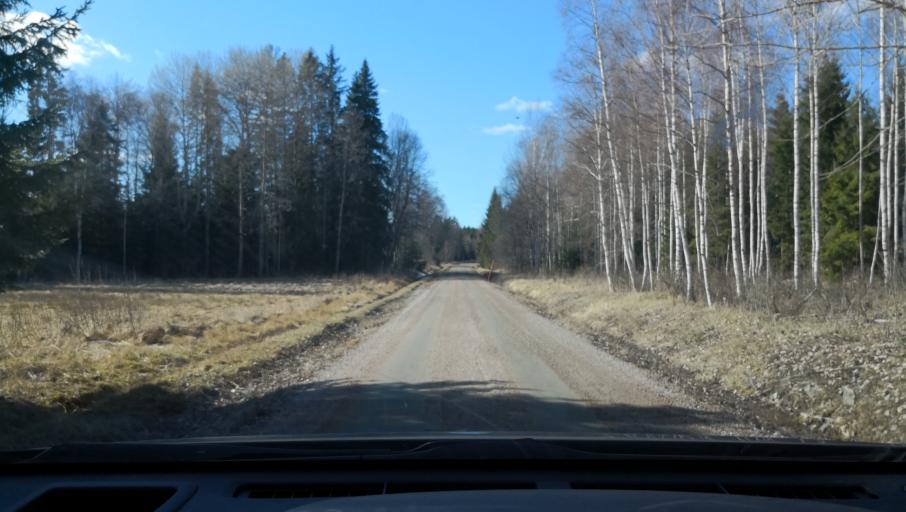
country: SE
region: Vaestmanland
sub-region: Sala Kommun
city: Sala
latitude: 60.1152
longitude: 16.6765
